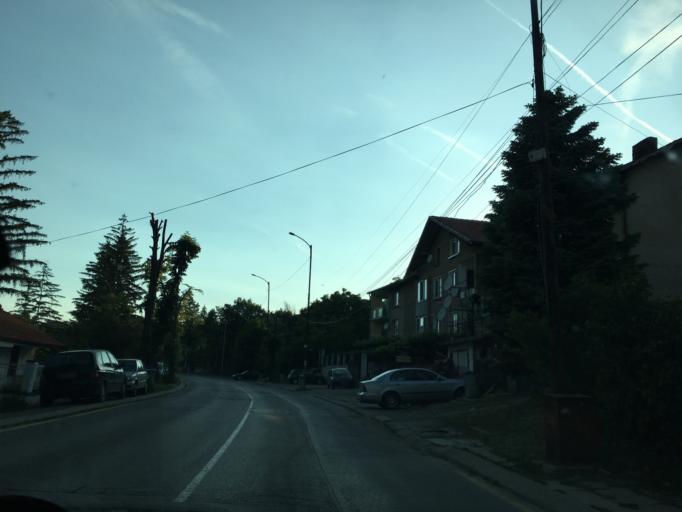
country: BG
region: Sofiya
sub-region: Obshtina Bozhurishte
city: Bozhurishte
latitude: 42.7127
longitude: 23.1611
